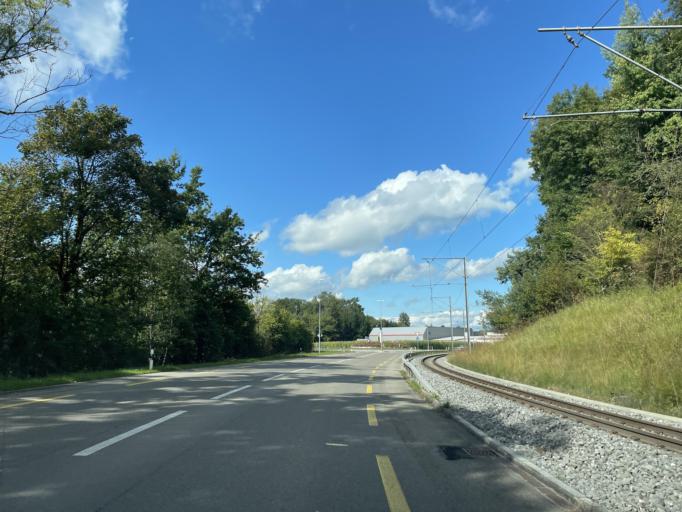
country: CH
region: Thurgau
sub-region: Frauenfeld District
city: Matzingen
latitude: 47.5123
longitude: 8.9393
